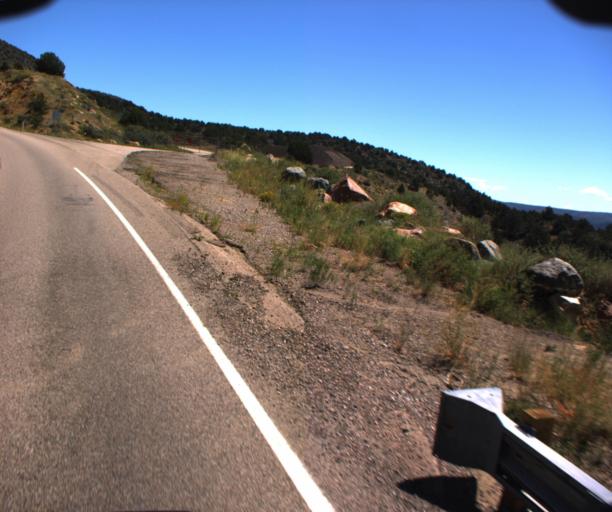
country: US
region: Arizona
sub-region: Gila County
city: San Carlos
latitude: 33.6512
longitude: -110.5703
